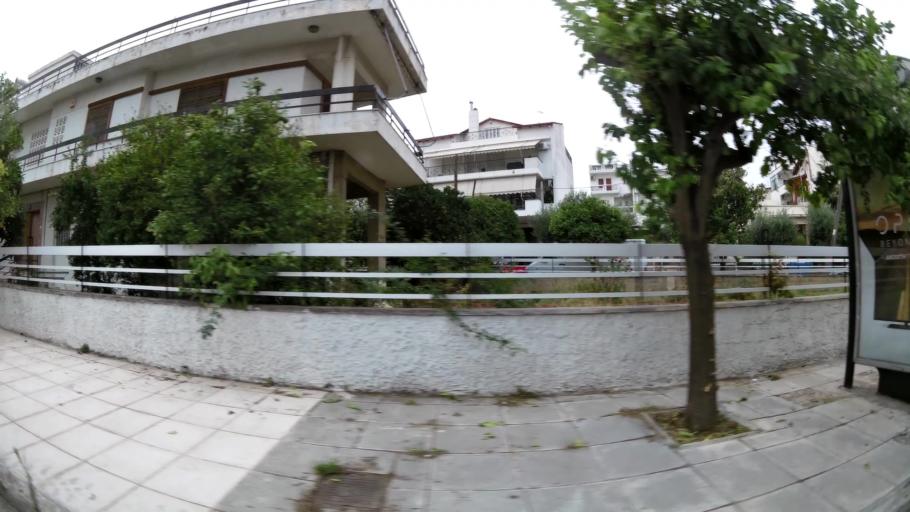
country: GR
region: Attica
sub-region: Nomarchia Athinas
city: Argyroupoli
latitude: 37.9121
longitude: 23.7417
